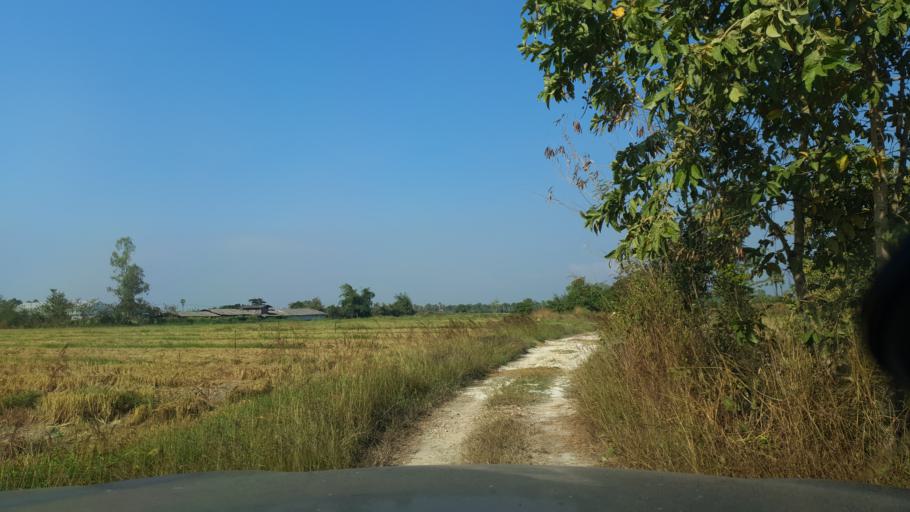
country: TH
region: Lamphun
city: Ban Thi
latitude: 18.6753
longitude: 99.1356
